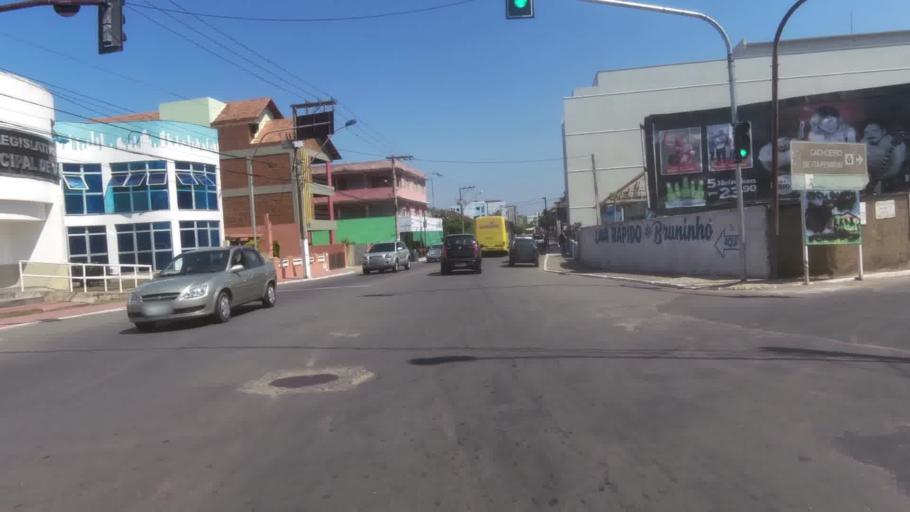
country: BR
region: Espirito Santo
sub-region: Marataizes
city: Marataizes
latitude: -21.0413
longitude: -40.8230
